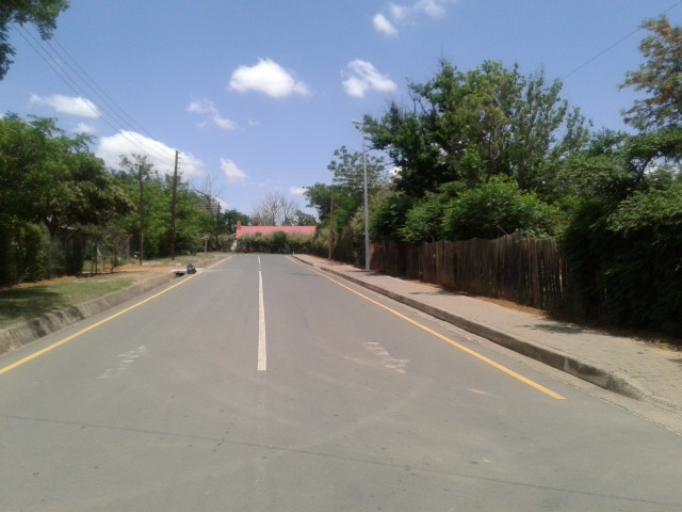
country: LS
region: Maseru
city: Maseru
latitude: -29.3038
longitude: 27.4715
